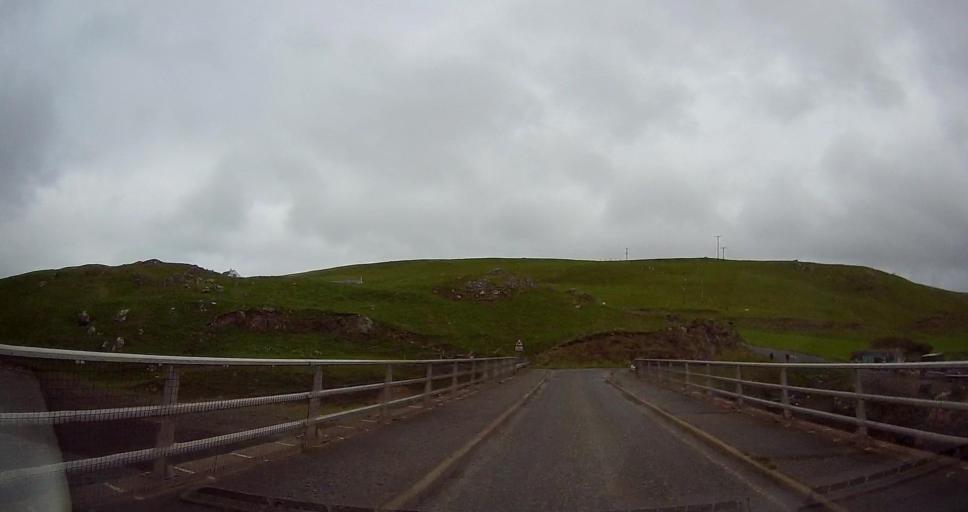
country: GB
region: Scotland
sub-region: Shetland Islands
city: Lerwick
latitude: 60.3769
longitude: -1.3834
